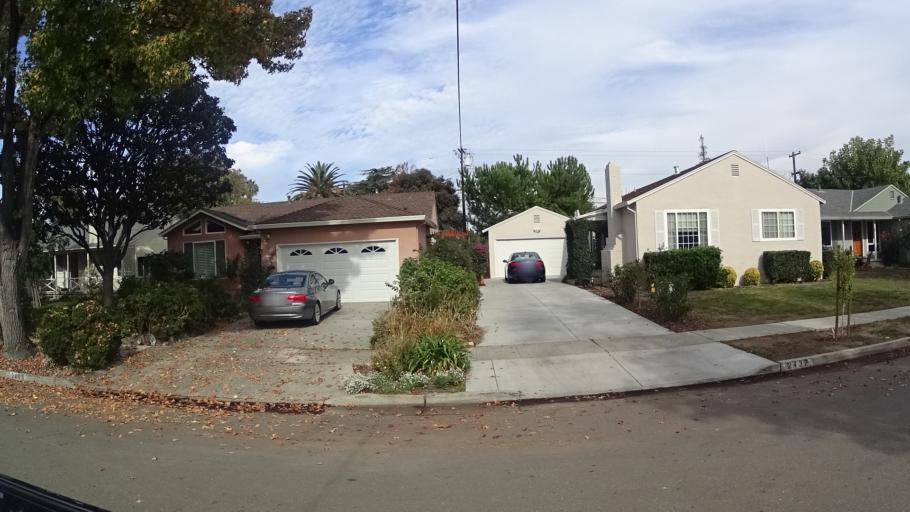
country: US
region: California
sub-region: Santa Clara County
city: Burbank
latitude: 37.3310
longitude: -121.9482
